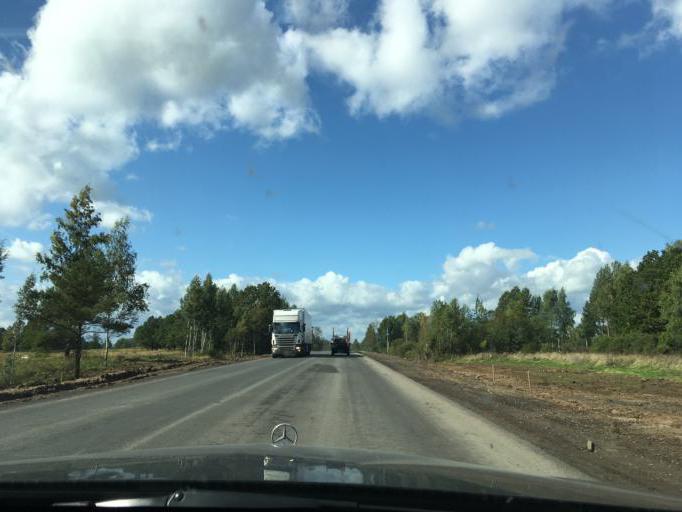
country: RU
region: Pskov
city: Velikiye Luki
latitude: 56.2709
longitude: 30.3678
